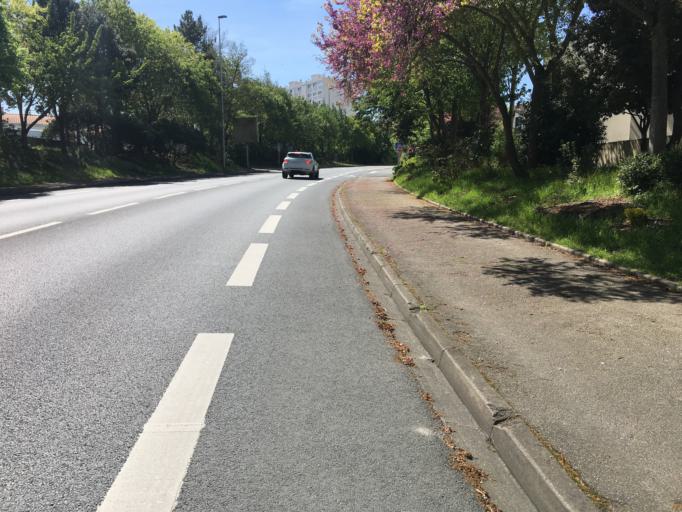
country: FR
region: Poitou-Charentes
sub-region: Departement de la Charente-Maritime
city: Aytre
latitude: 46.1415
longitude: -1.1406
